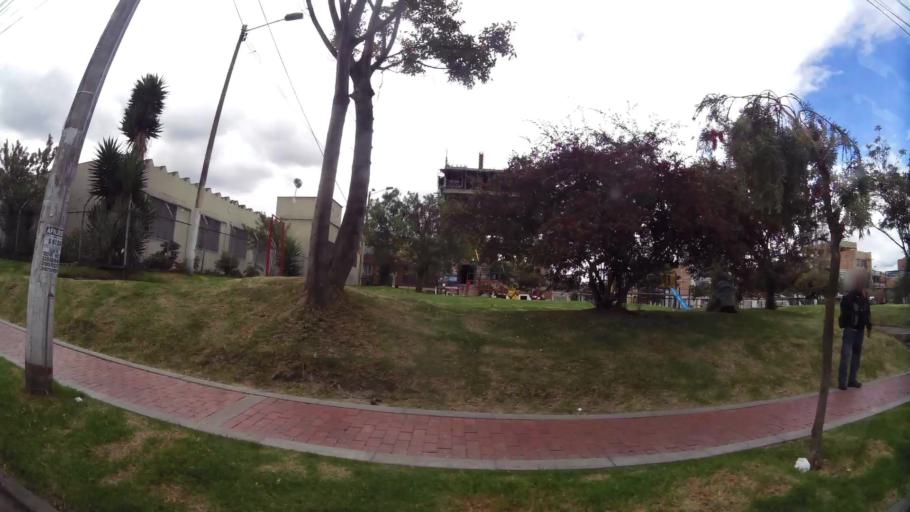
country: CO
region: Bogota D.C.
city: Bogota
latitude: 4.6062
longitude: -74.1303
